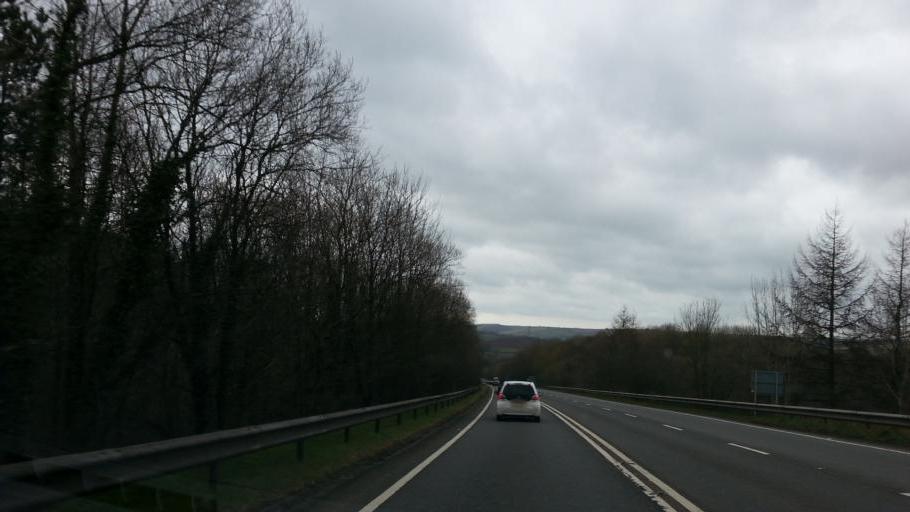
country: GB
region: England
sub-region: Devon
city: South Molton
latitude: 51.0108
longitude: -3.7552
